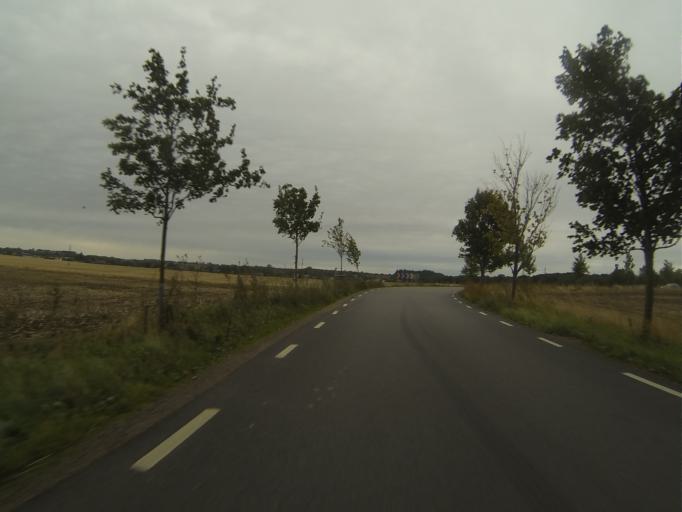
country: SE
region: Skane
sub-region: Lunds Kommun
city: Genarp
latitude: 55.6348
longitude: 13.4074
